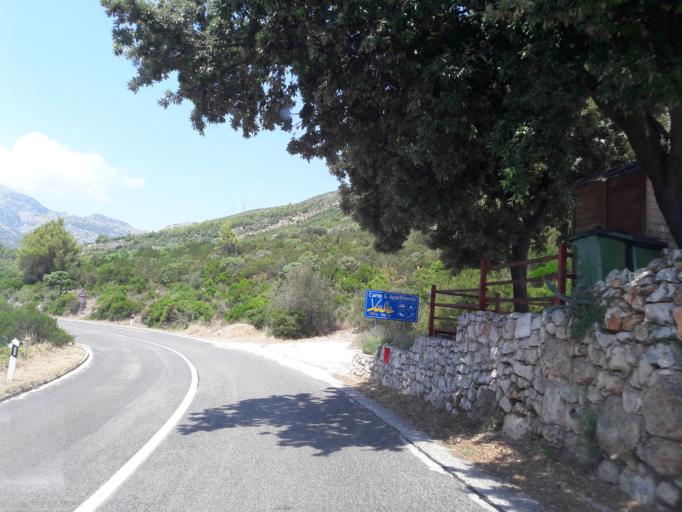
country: HR
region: Dubrovacko-Neretvanska
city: Orebic
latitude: 42.9766
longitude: 17.2302
